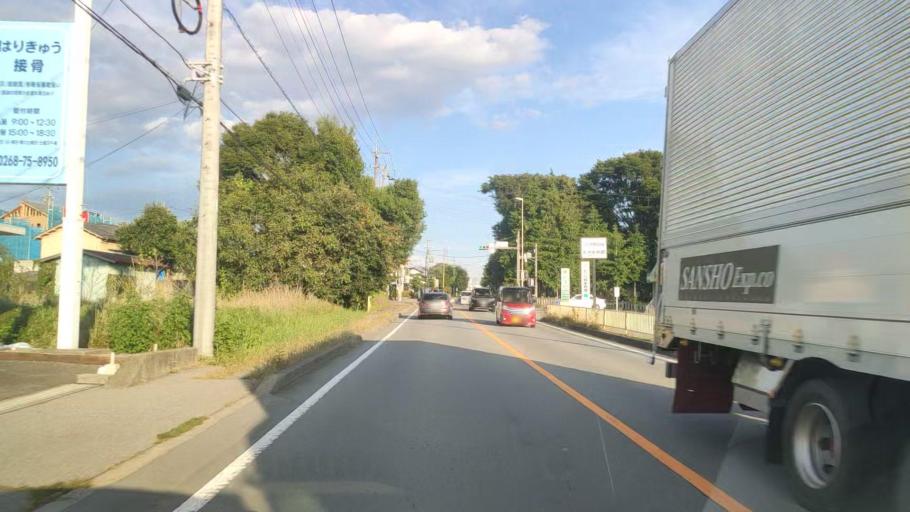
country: JP
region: Nagano
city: Ueda
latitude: 36.3555
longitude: 138.3418
